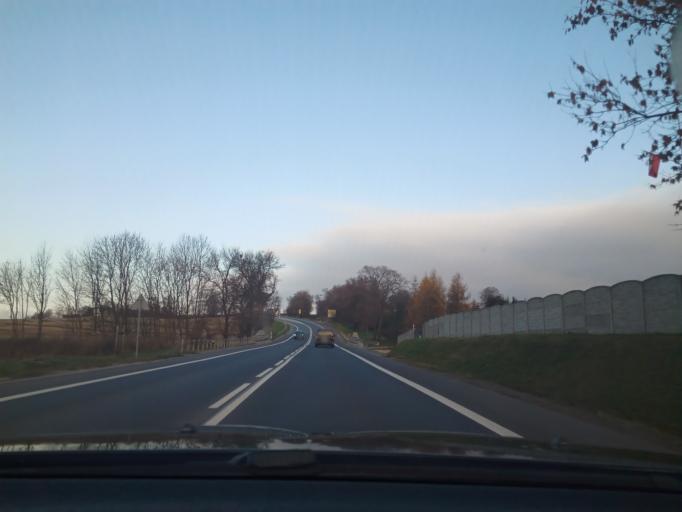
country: PL
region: Lesser Poland Voivodeship
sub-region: Powiat krakowski
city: Slomniki
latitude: 50.2890
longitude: 20.0490
